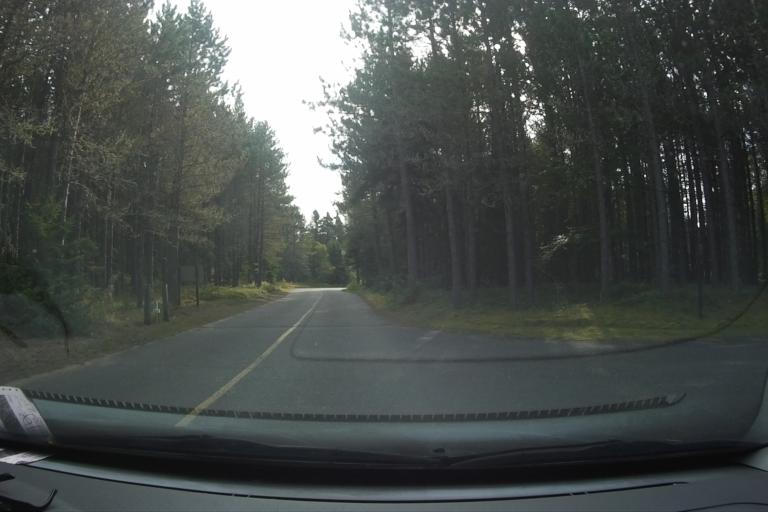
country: CA
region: Ontario
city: Marathon
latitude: 48.7862
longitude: -86.6202
